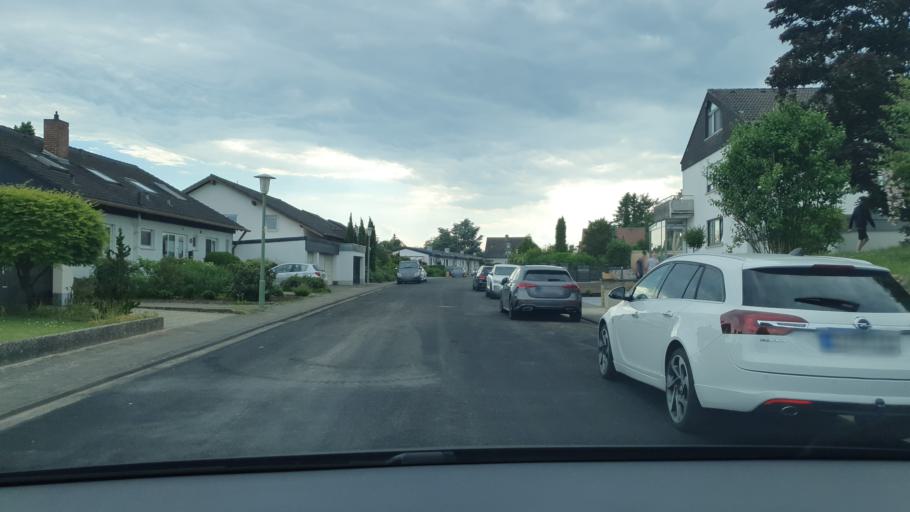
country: DE
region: Rheinland-Pfalz
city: Kaiserslautern
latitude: 49.4677
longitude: 7.7704
